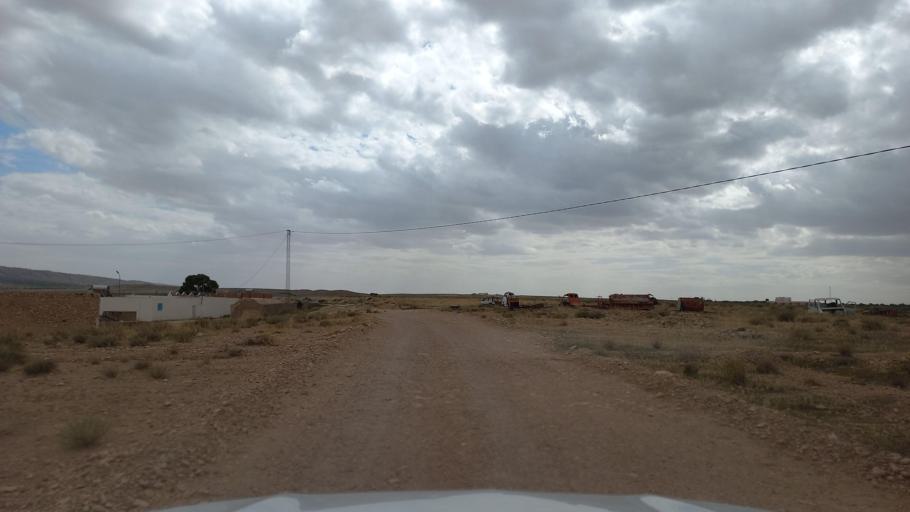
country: TN
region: Al Qasrayn
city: Sbiba
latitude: 35.3799
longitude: 9.1183
